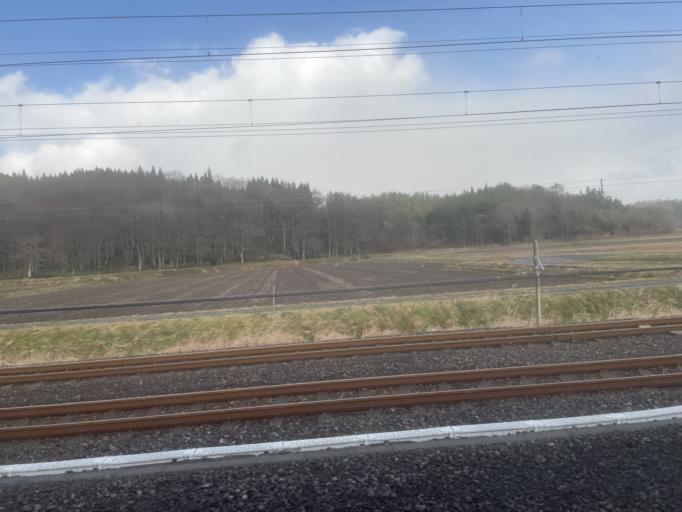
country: JP
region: Aomori
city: Aomori Shi
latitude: 41.0634
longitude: 140.5754
